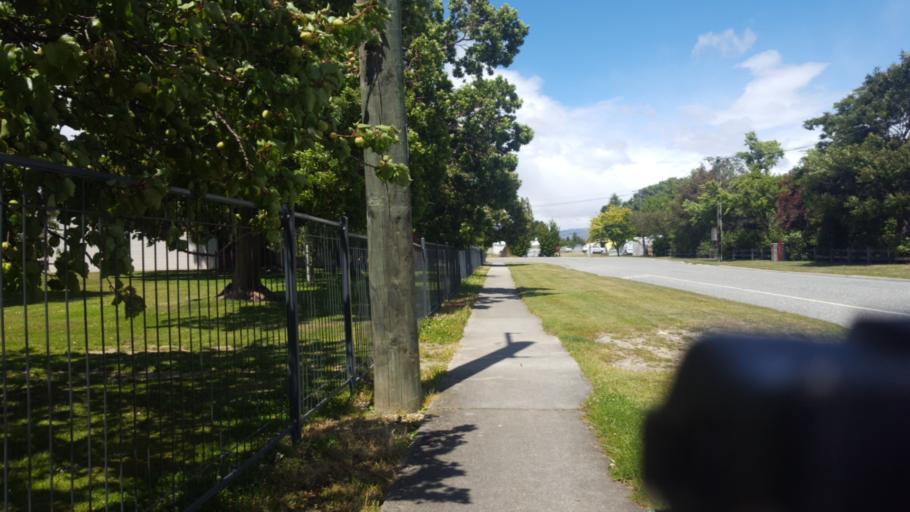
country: NZ
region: Otago
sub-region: Queenstown-Lakes District
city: Wanaka
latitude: -45.1915
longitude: 169.3184
